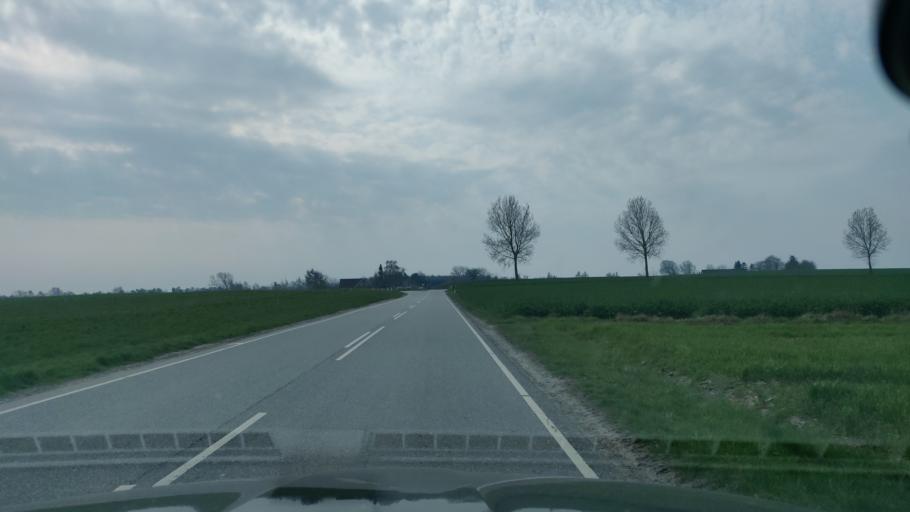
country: DK
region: South Denmark
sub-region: Nordfyns Kommune
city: Sonderso
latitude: 55.4986
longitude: 10.2488
